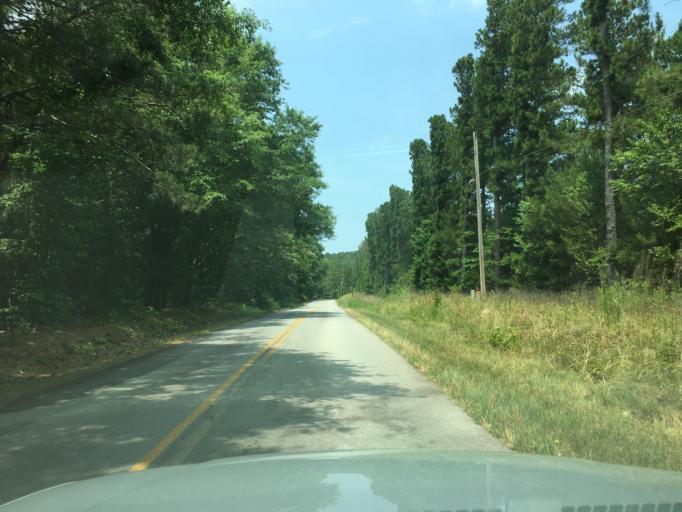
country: US
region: Georgia
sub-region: Hart County
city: Hartwell
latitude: 34.3464
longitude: -82.9040
